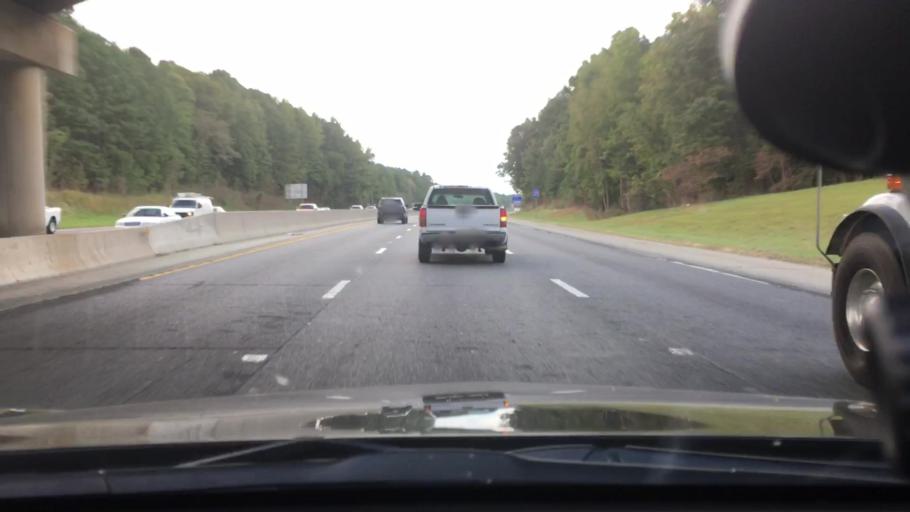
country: US
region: North Carolina
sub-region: Orange County
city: Chapel Hill
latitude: 35.9450
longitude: -78.9945
